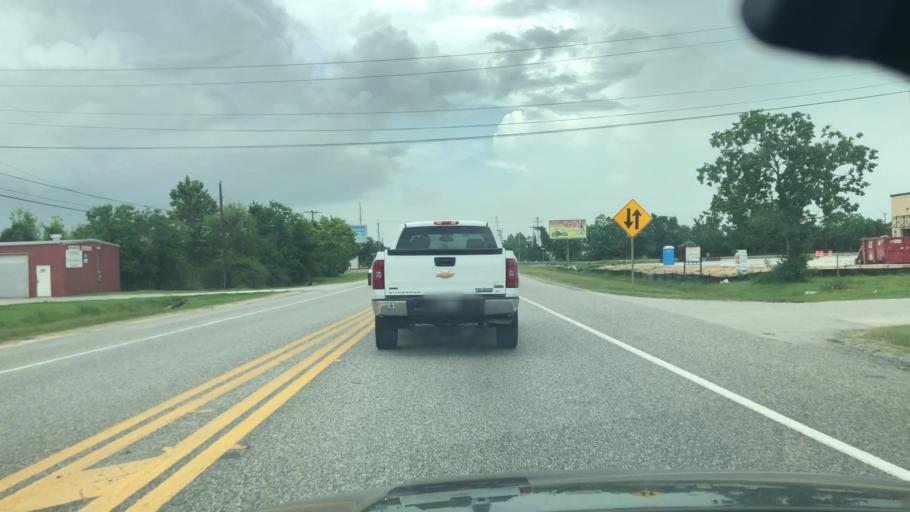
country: US
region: Texas
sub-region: Galveston County
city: Dickinson
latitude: 29.4819
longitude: -95.0678
